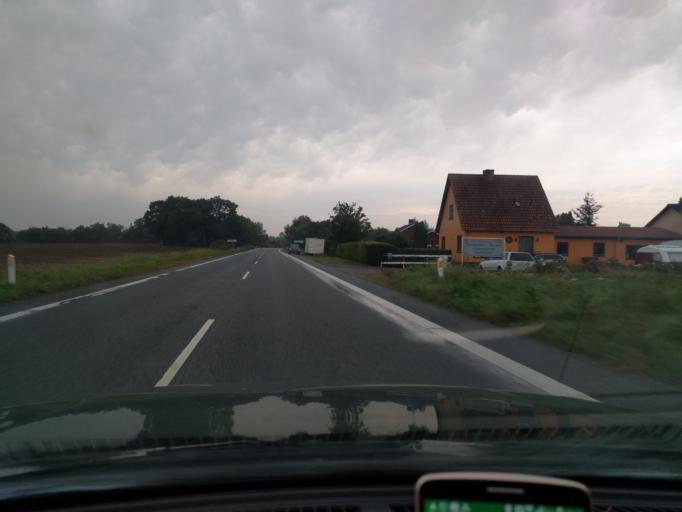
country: DK
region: Zealand
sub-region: Guldborgsund Kommune
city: Norre Alslev
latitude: 54.9045
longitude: 11.8739
